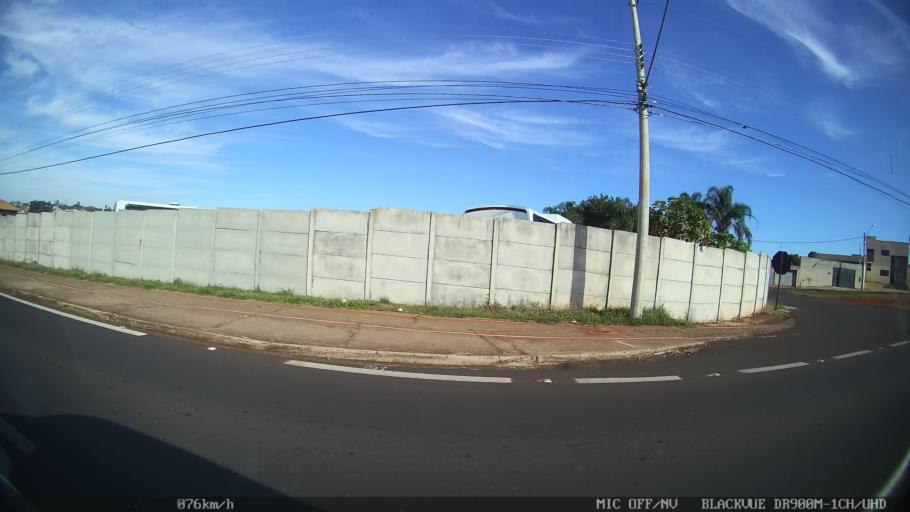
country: BR
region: Sao Paulo
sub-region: Araraquara
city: Araraquara
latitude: -21.7908
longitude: -48.1487
